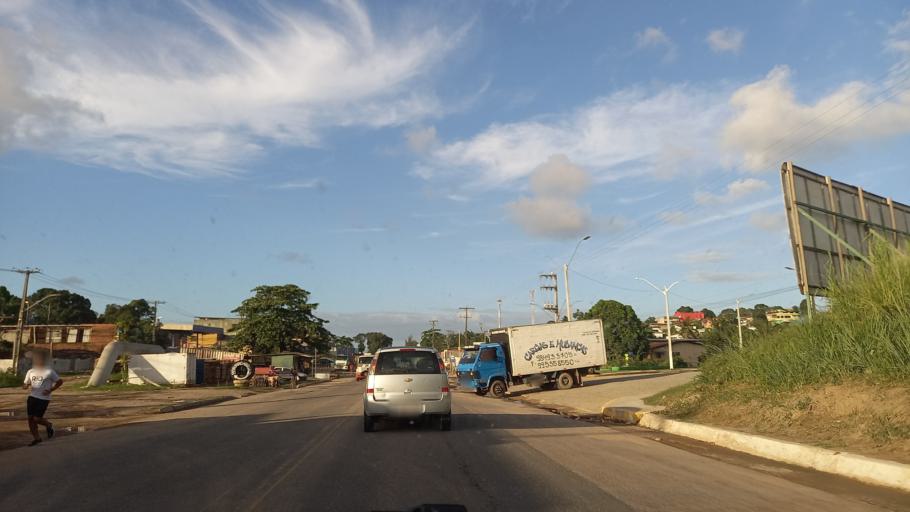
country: BR
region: Pernambuco
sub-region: Cabo De Santo Agostinho
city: Cabo
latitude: -8.2414
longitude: -34.9876
